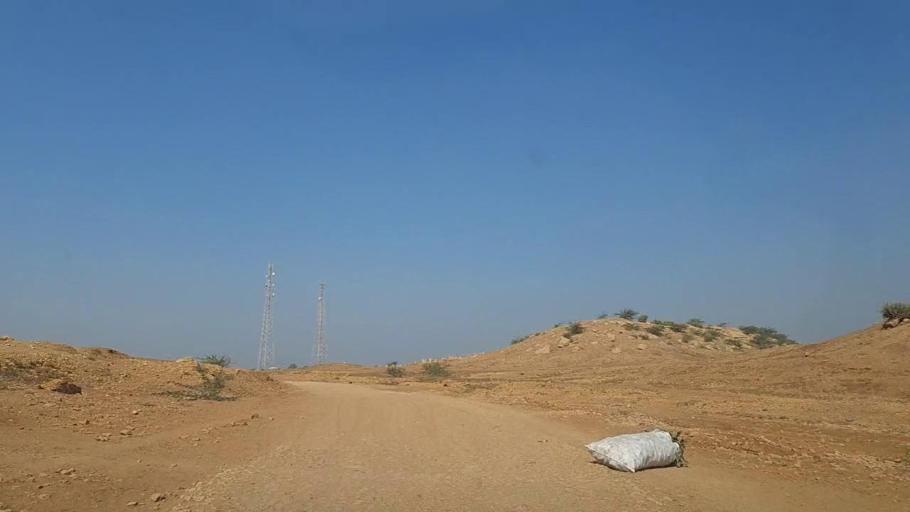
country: PK
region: Sindh
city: Daro Mehar
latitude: 24.8956
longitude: 68.0674
